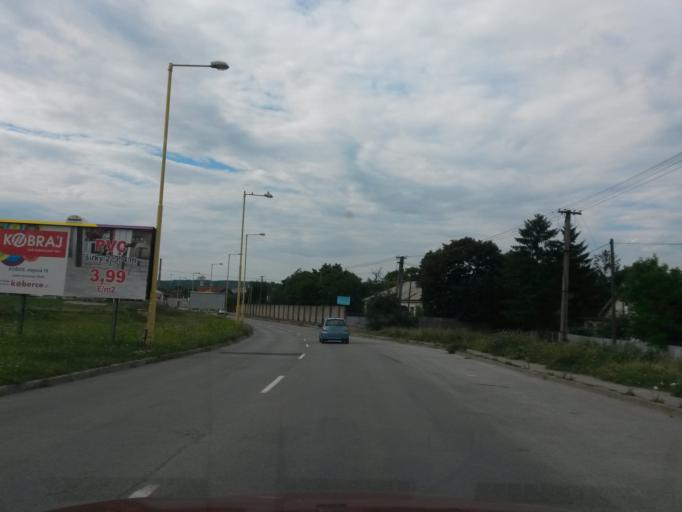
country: SK
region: Kosicky
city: Kosice
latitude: 48.7359
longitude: 21.2680
